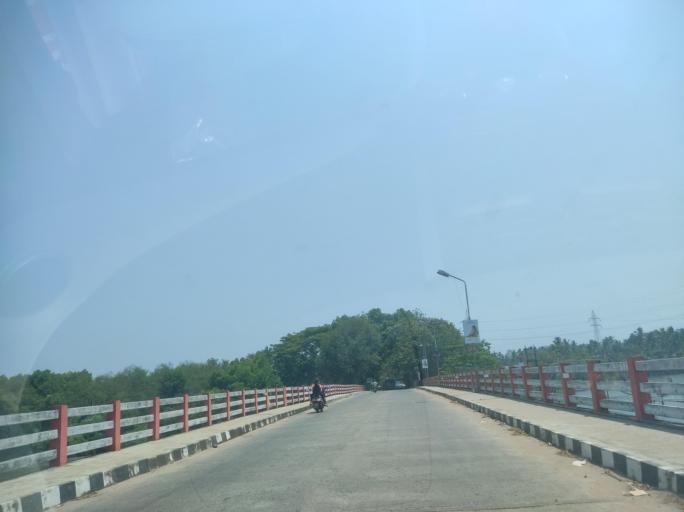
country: IN
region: Kerala
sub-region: Ernakulam
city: Cochin
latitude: 9.9009
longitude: 76.2826
